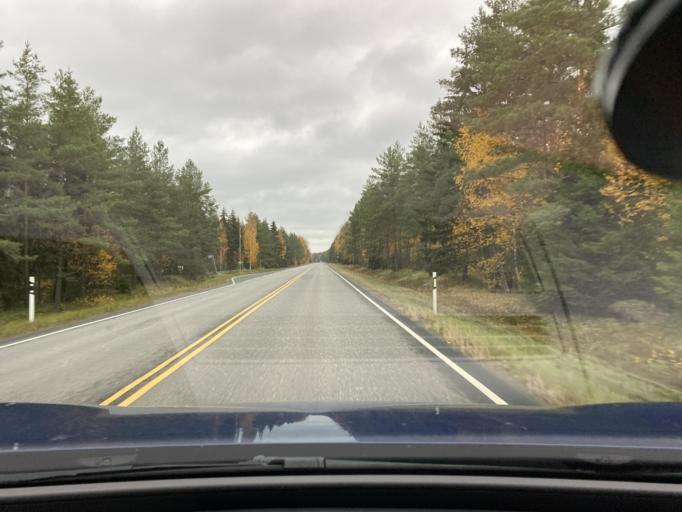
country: FI
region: Varsinais-Suomi
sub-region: Loimaa
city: Ylaene
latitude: 60.9088
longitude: 22.4111
